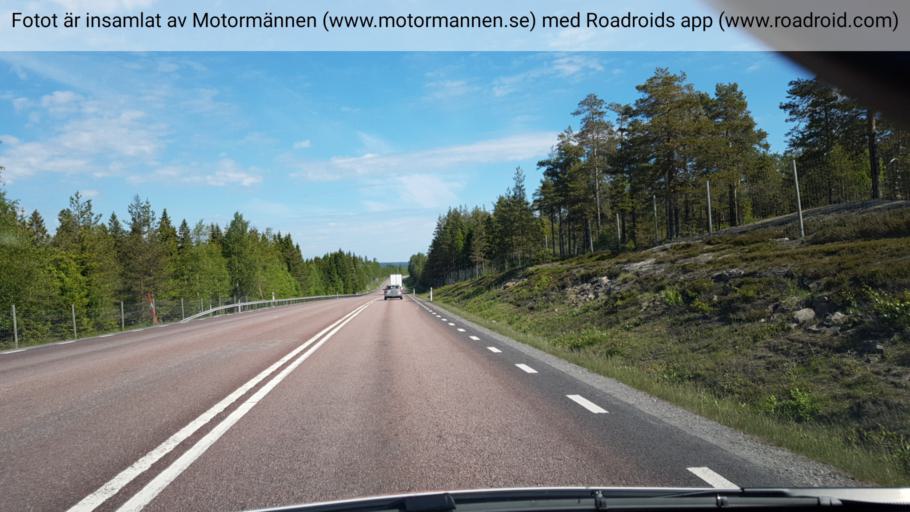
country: SE
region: Vaesterbotten
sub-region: Skelleftea Kommun
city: Burea
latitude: 64.4454
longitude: 21.2832
